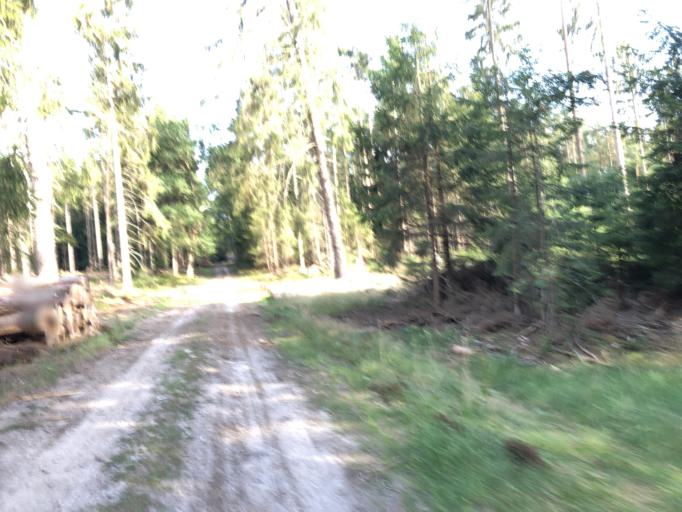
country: DE
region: Lower Saxony
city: Thomasburg
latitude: 53.2119
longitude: 10.6582
